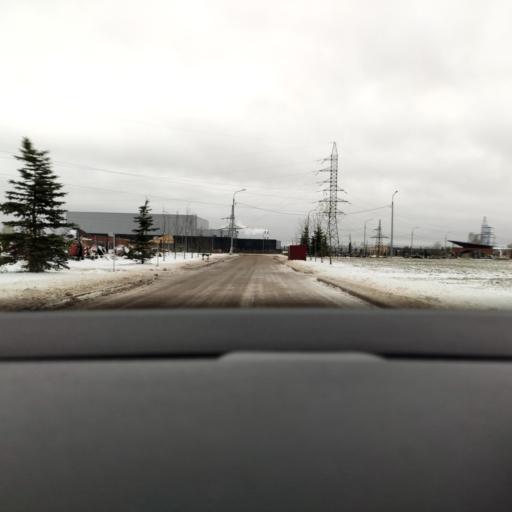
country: RU
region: Moskovskaya
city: Alabushevo
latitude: 56.0139
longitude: 37.1376
